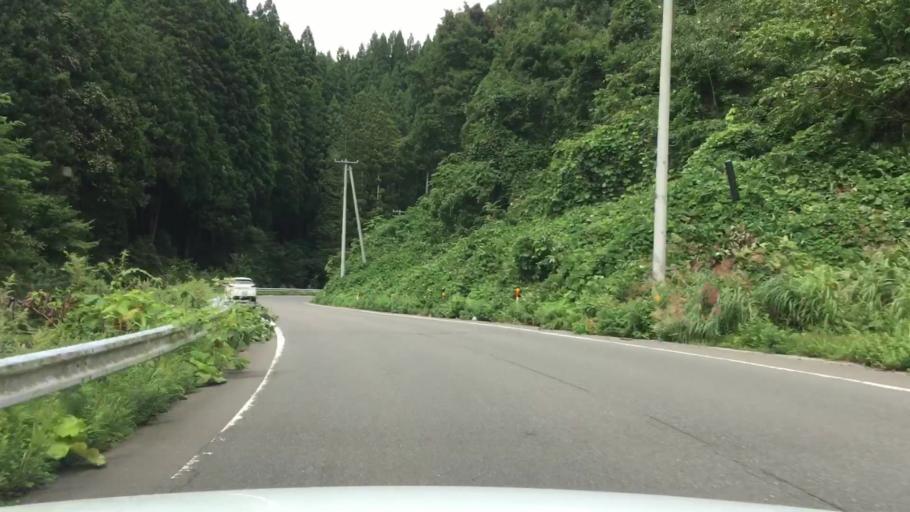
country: JP
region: Aomori
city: Shimokizukuri
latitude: 40.7334
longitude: 140.2509
